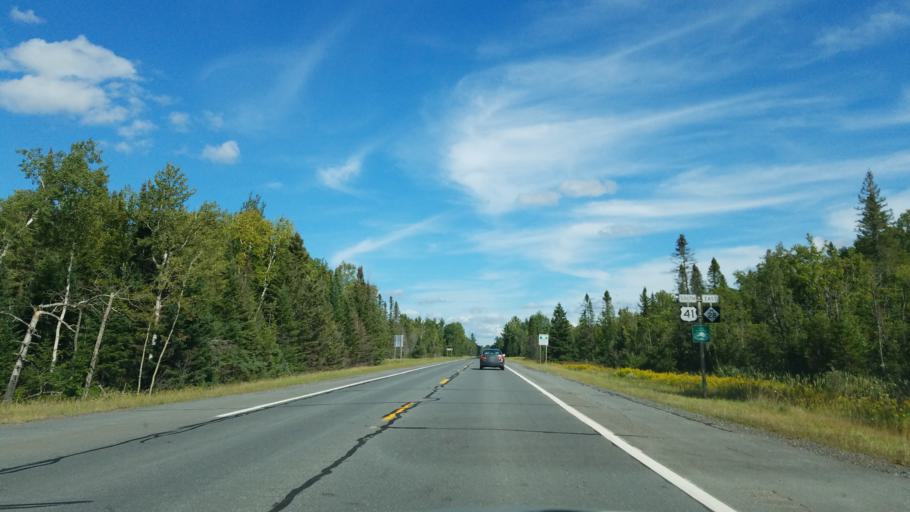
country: US
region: Michigan
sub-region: Baraga County
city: L'Anse
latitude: 46.5789
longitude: -88.3965
